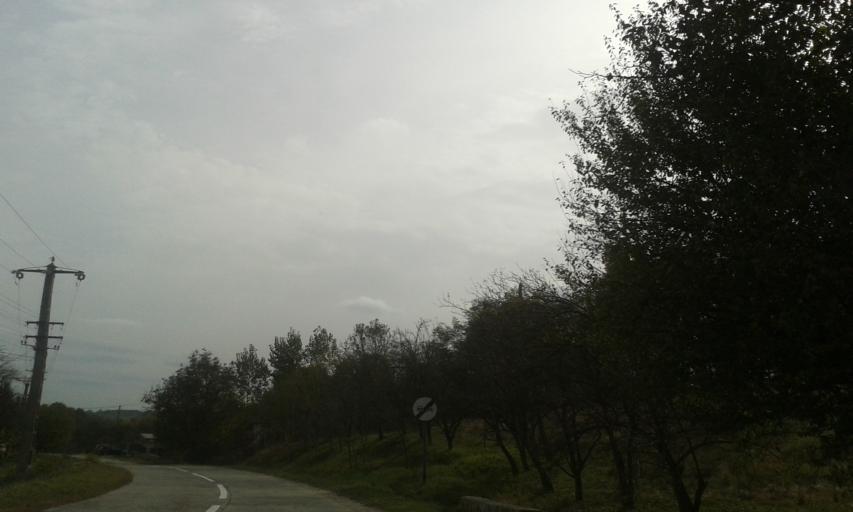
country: RO
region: Valcea
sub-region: Comuna Gradistea
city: Gradistea
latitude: 44.9146
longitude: 23.7807
